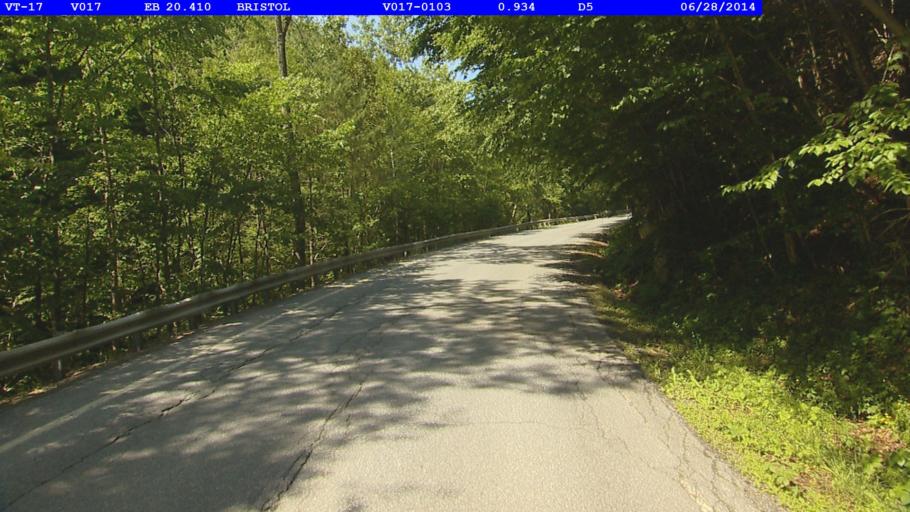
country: US
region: Vermont
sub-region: Addison County
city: Bristol
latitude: 44.1570
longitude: -73.0418
